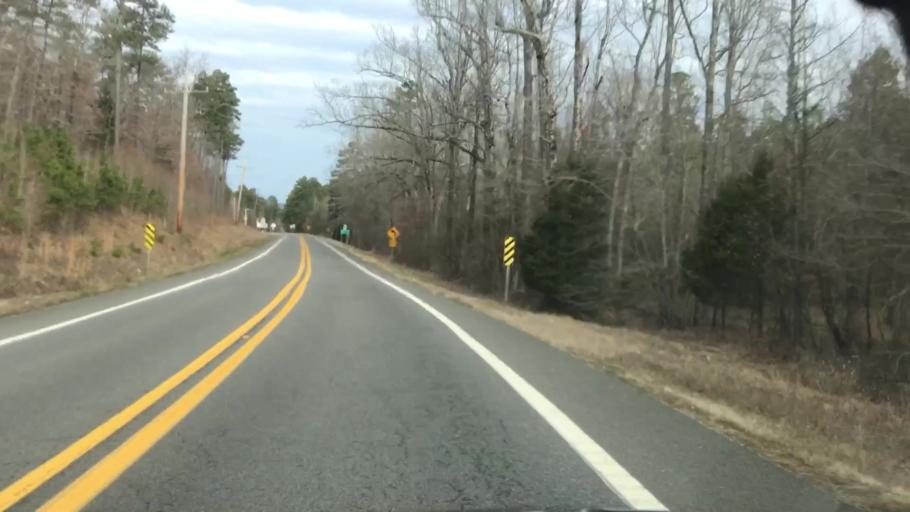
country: US
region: Arkansas
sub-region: Montgomery County
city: Mount Ida
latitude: 34.6064
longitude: -93.6719
